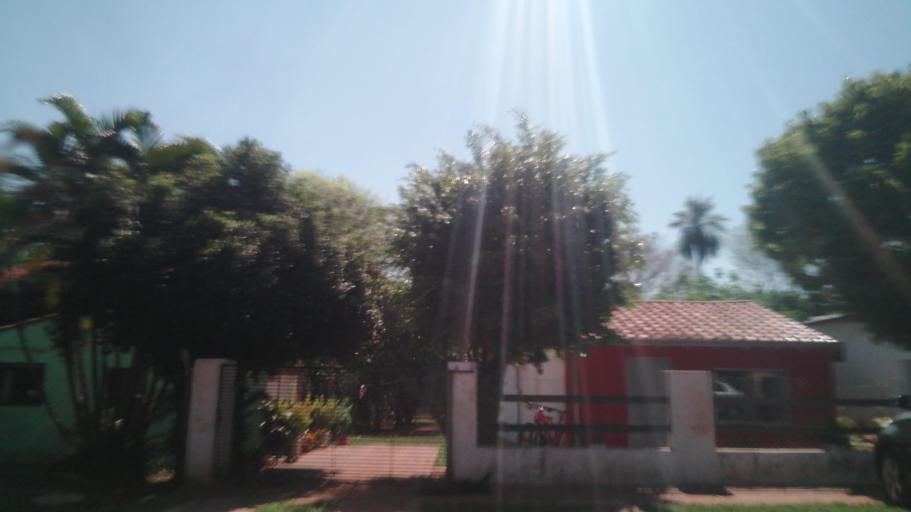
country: PY
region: Misiones
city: San Juan Bautista
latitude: -26.6641
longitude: -57.1509
